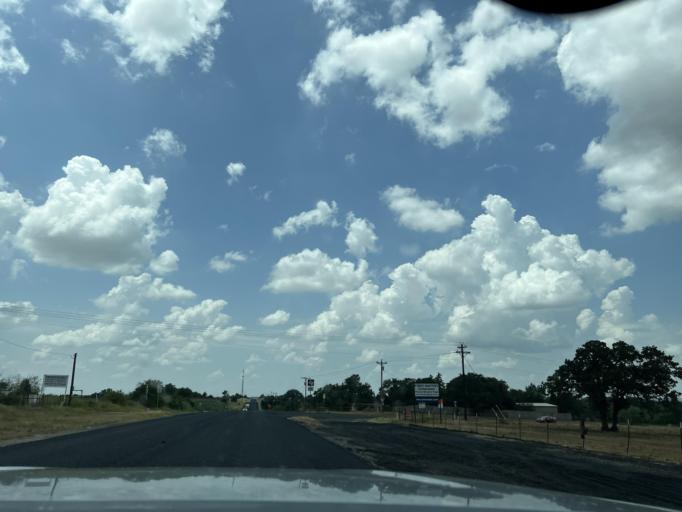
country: US
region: Texas
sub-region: Wise County
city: Boyd
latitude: 33.0761
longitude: -97.6491
